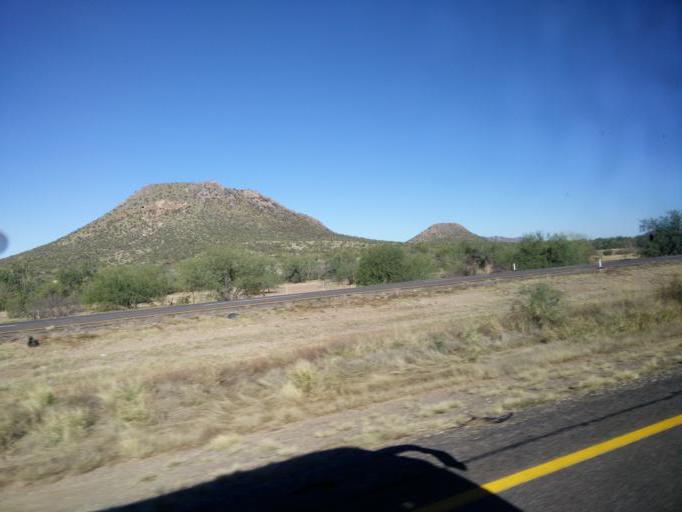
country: MX
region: Sonora
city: Hermosillo
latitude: 28.8902
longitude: -110.9540
